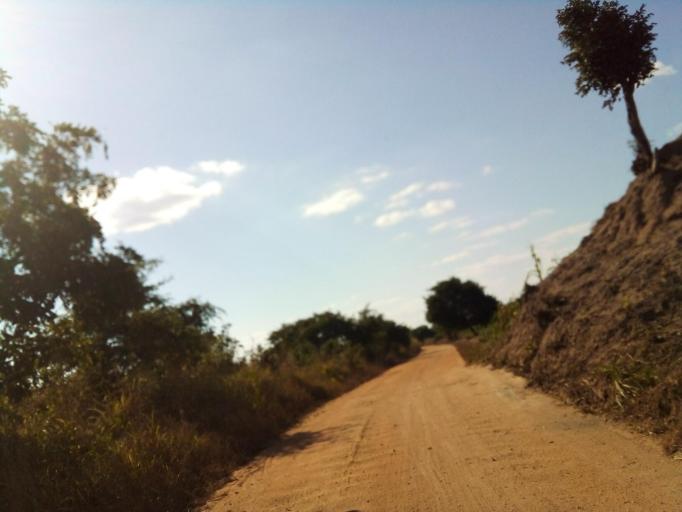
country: MZ
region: Zambezia
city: Quelimane
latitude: -17.5587
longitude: 36.6357
